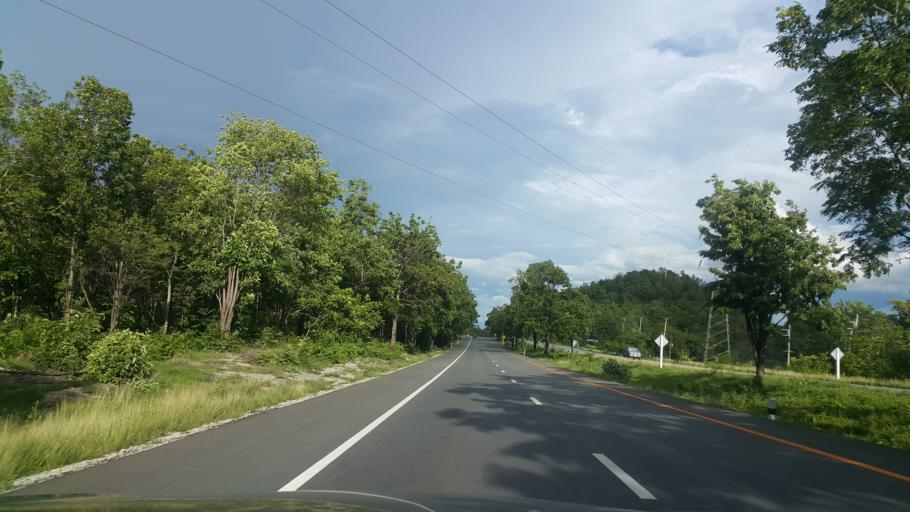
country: TH
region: Tak
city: Ban Tak
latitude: 16.9785
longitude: 99.1246
